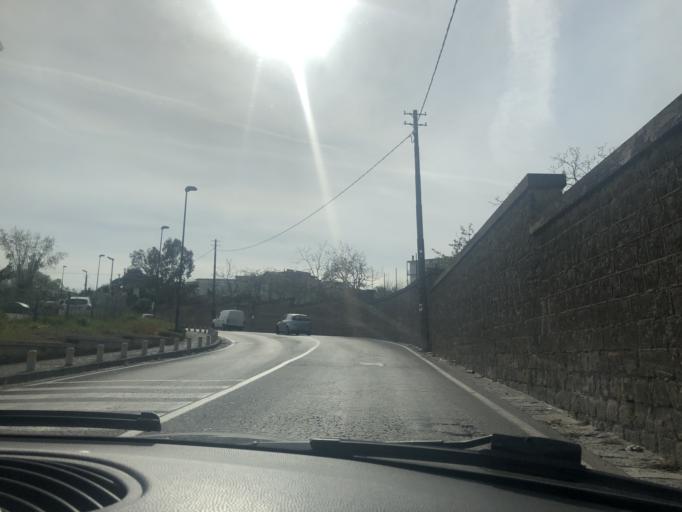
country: IT
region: Campania
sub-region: Provincia di Napoli
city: Torre Caracciolo
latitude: 40.8683
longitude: 14.2048
